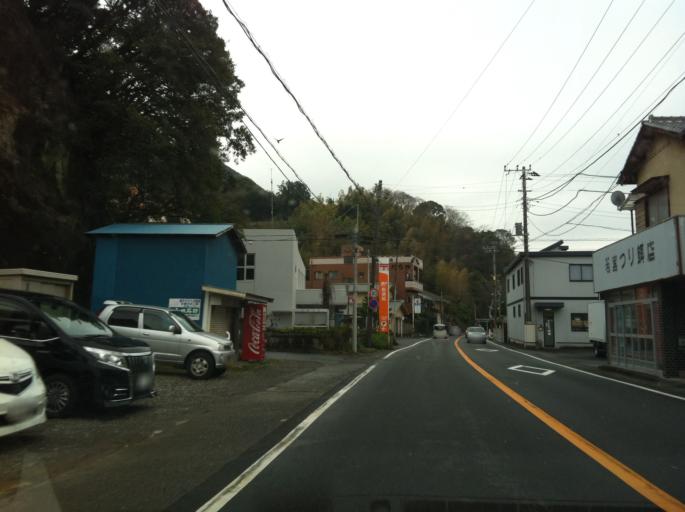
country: JP
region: Shizuoka
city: Numazu
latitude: 35.0439
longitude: 138.9015
